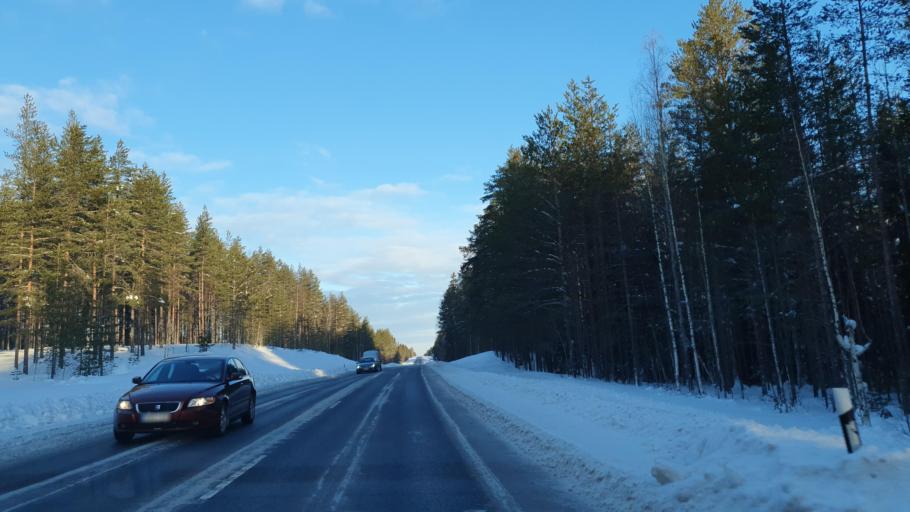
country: FI
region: Kainuu
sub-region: Kajaani
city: Vuolijoki
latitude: 64.4901
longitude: 27.3201
